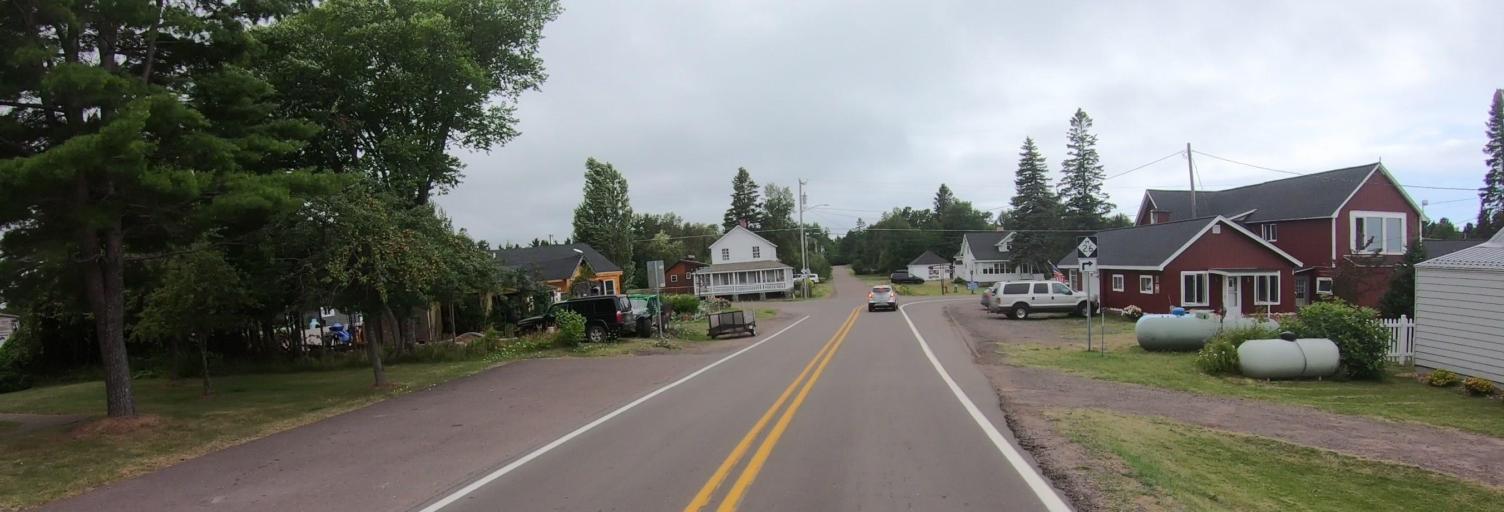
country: US
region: Michigan
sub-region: Keweenaw County
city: Eagle River
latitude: 47.4550
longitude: -88.1597
